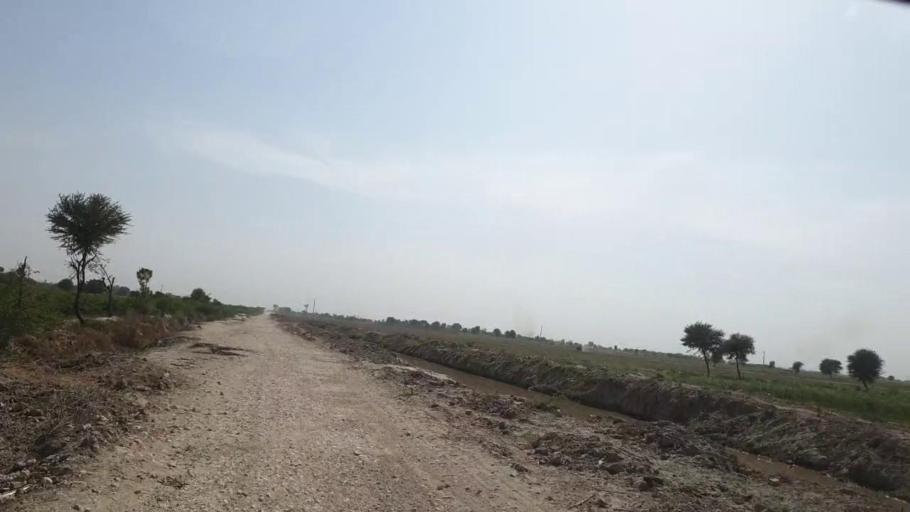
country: PK
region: Sindh
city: Nabisar
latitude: 25.0865
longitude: 69.5807
